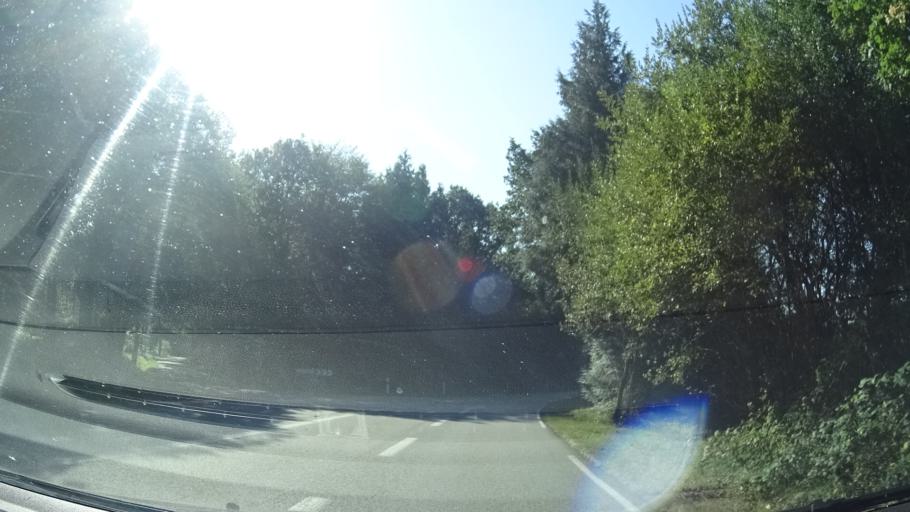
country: FR
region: Brittany
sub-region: Departement du Finistere
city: Cast
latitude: 48.1709
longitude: -4.1230
